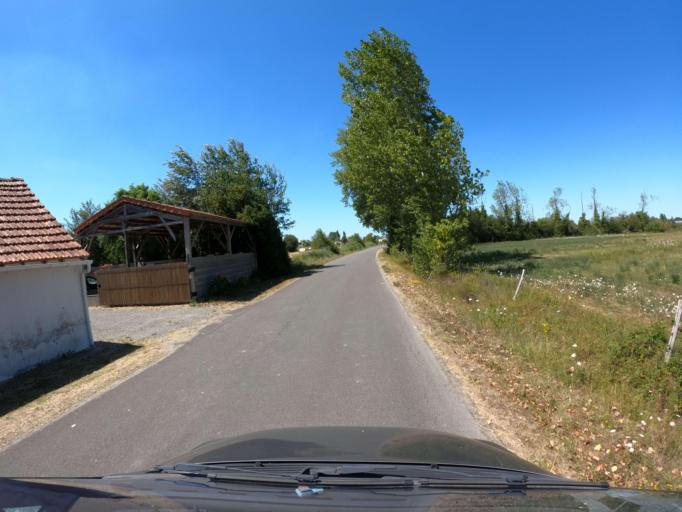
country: FR
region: Pays de la Loire
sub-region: Departement de la Vendee
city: Saint-Jean-de-Monts
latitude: 46.8043
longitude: -2.0910
